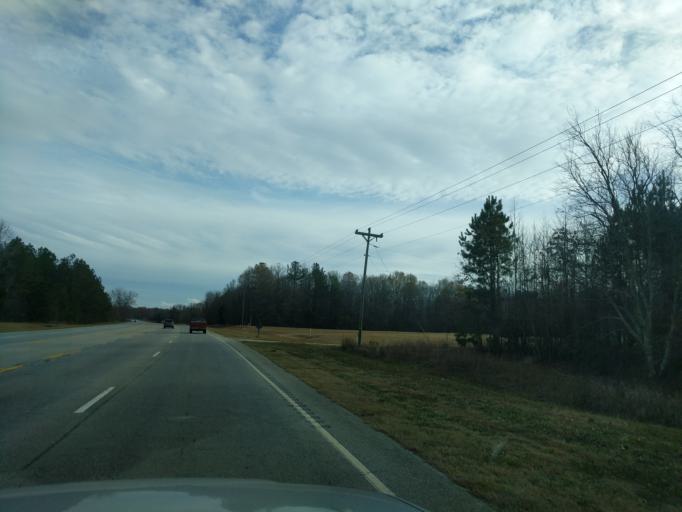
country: US
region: South Carolina
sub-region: Anderson County
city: Williamston
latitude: 34.6139
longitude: -82.3767
